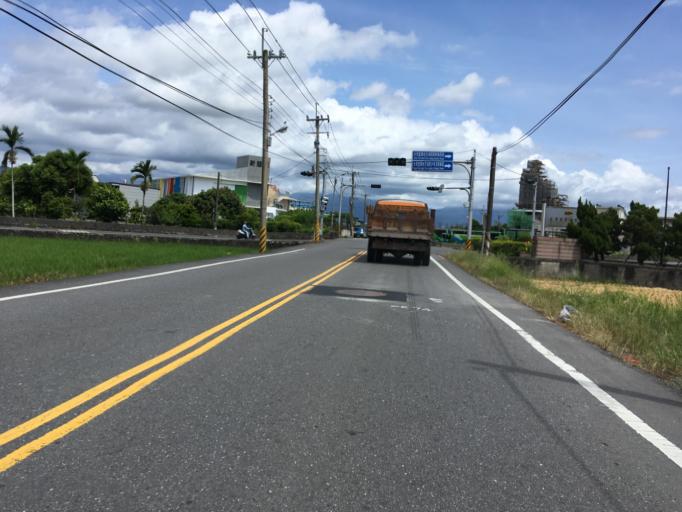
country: TW
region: Taiwan
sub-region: Yilan
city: Yilan
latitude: 24.6951
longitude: 121.7660
